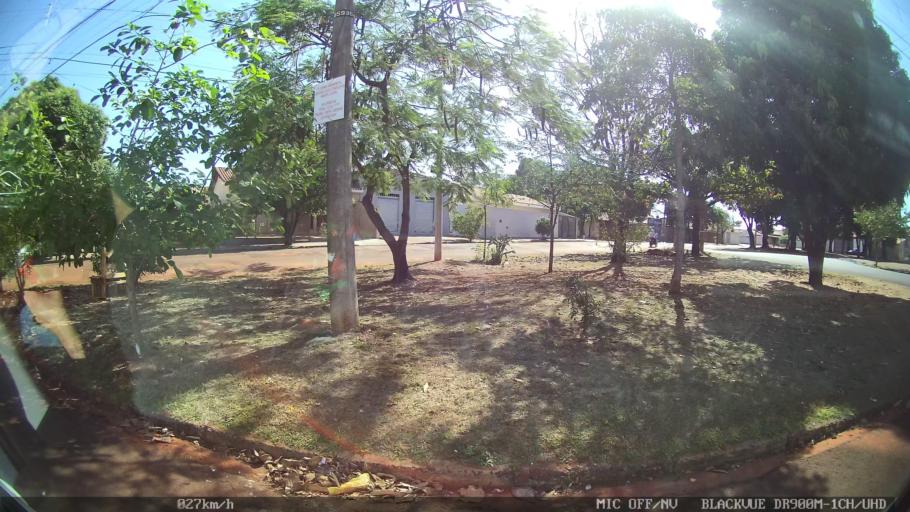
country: BR
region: Sao Paulo
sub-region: Sao Jose Do Rio Preto
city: Sao Jose do Rio Preto
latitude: -20.7854
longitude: -49.4002
